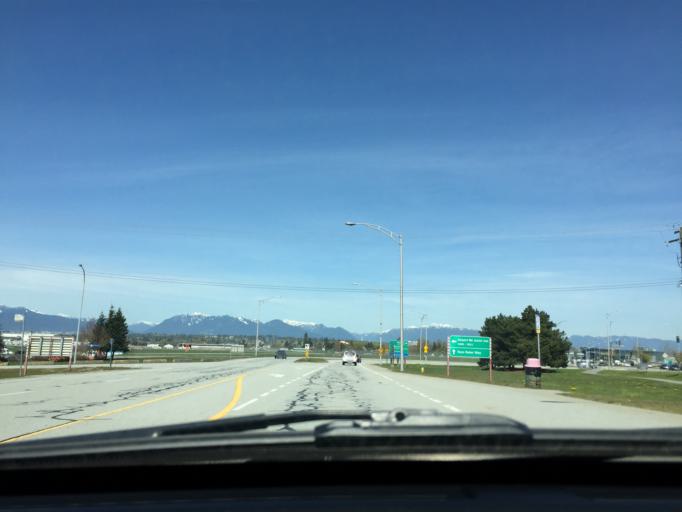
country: CA
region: British Columbia
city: Richmond
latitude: 49.1787
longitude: -123.1555
